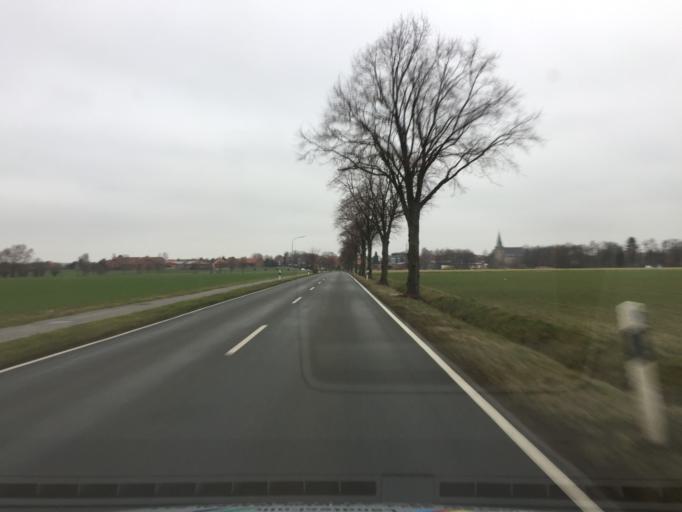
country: DE
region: Lower Saxony
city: Meerbeck
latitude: 52.3361
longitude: 9.1467
